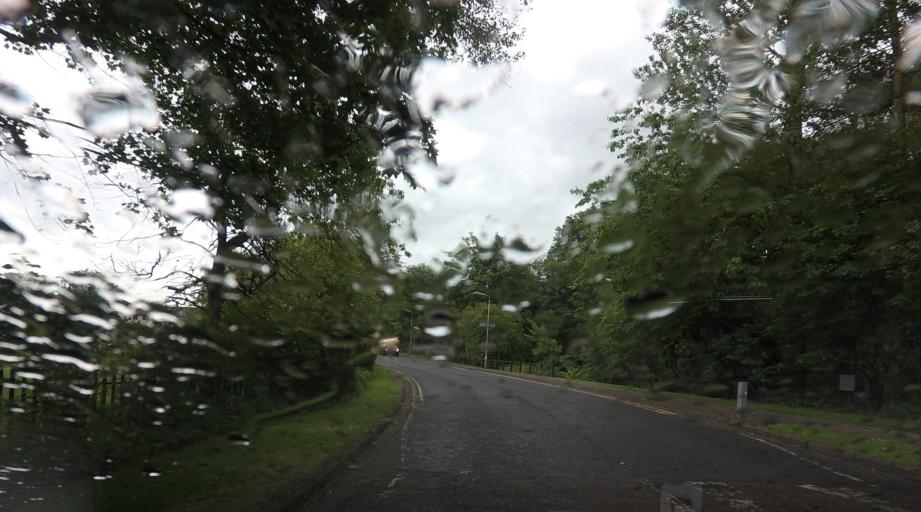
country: GB
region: Scotland
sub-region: Fife
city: Ballingry
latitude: 56.1486
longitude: -3.3273
